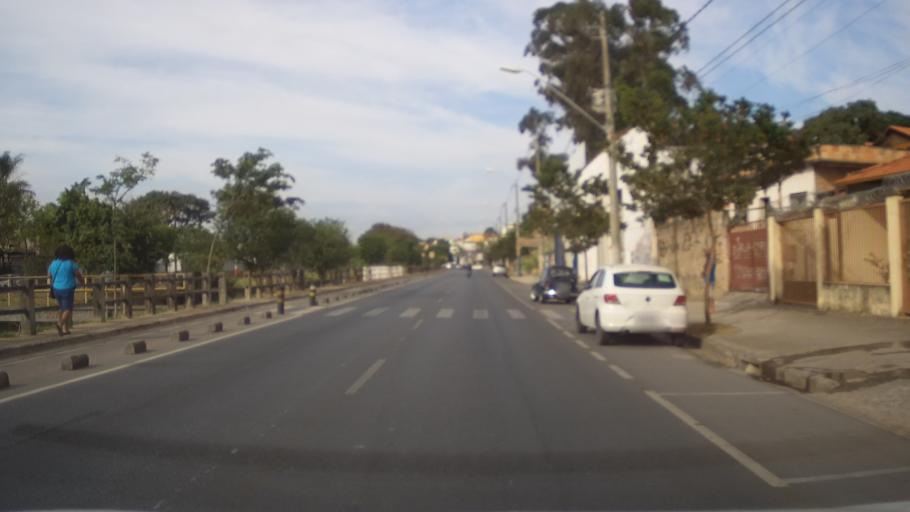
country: BR
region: Minas Gerais
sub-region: Contagem
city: Contagem
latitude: -19.8669
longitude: -44.0092
